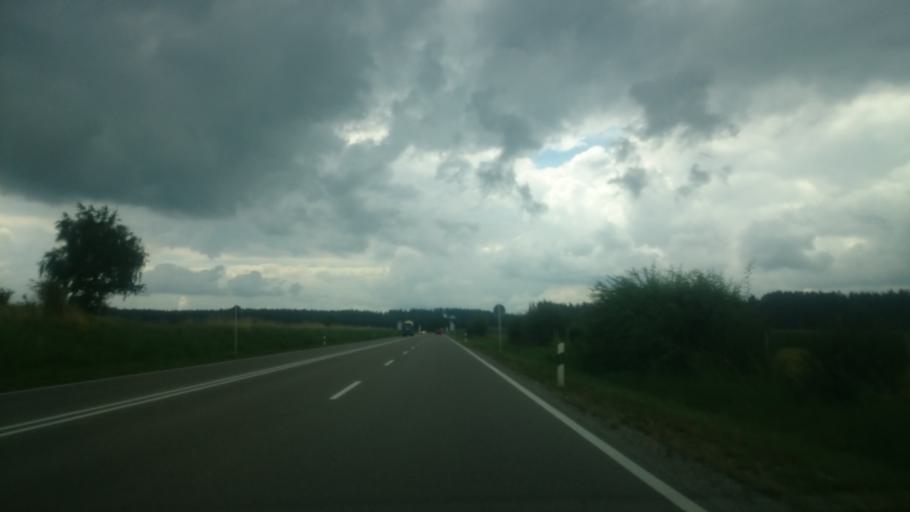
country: DE
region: Bavaria
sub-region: Swabia
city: Rieden
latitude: 47.9195
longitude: 10.6587
